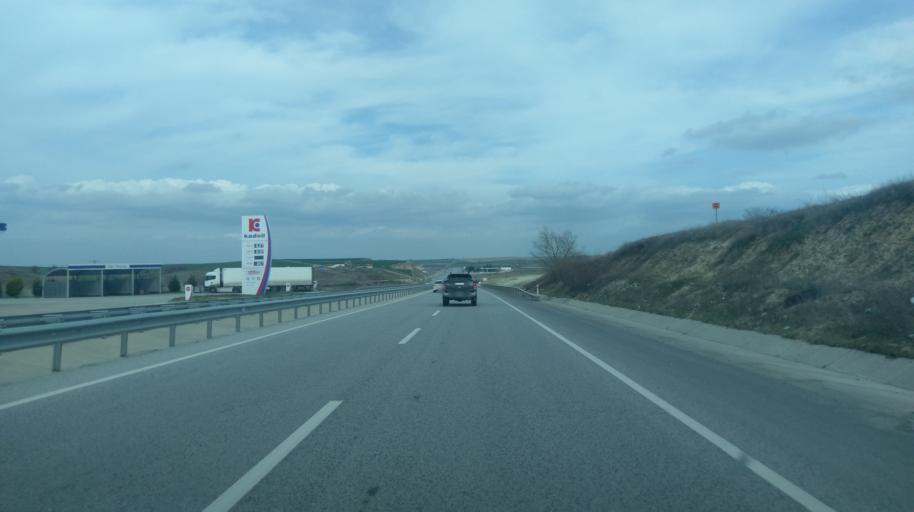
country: TR
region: Edirne
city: Kircasalih
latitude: 41.4034
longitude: 26.8139
